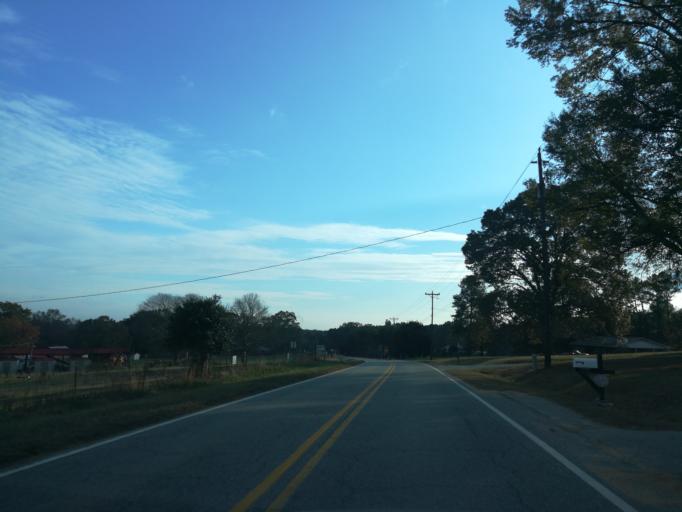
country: US
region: North Carolina
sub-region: Durham County
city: Durham
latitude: 35.9931
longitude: -78.9940
